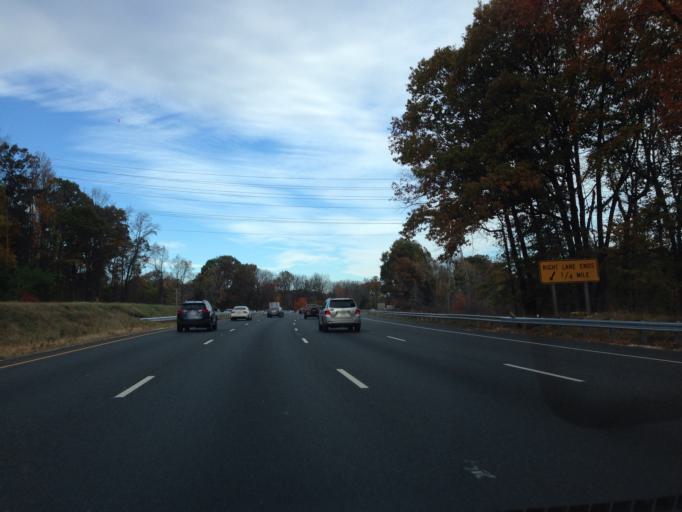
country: US
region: Maryland
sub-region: Baltimore County
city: Lutherville
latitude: 39.3772
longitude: -76.6578
